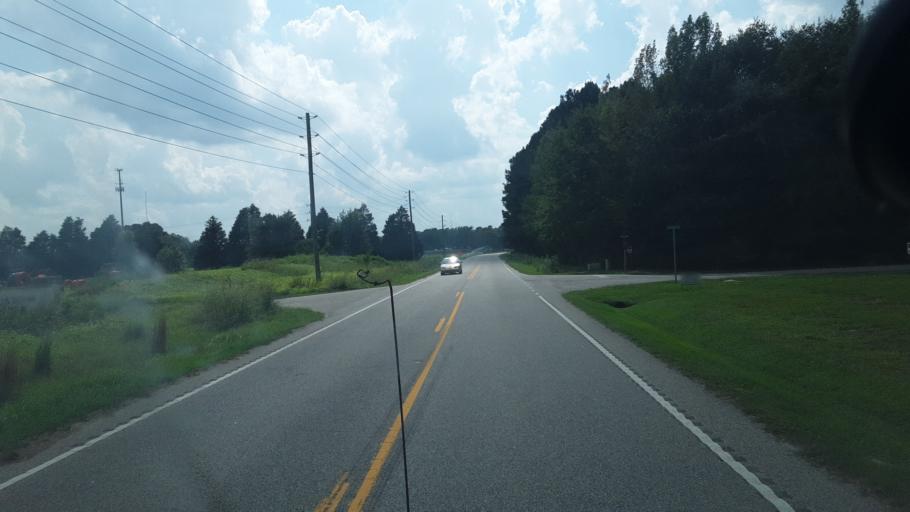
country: US
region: South Carolina
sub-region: Sumter County
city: Sumter
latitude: 33.9636
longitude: -80.3700
